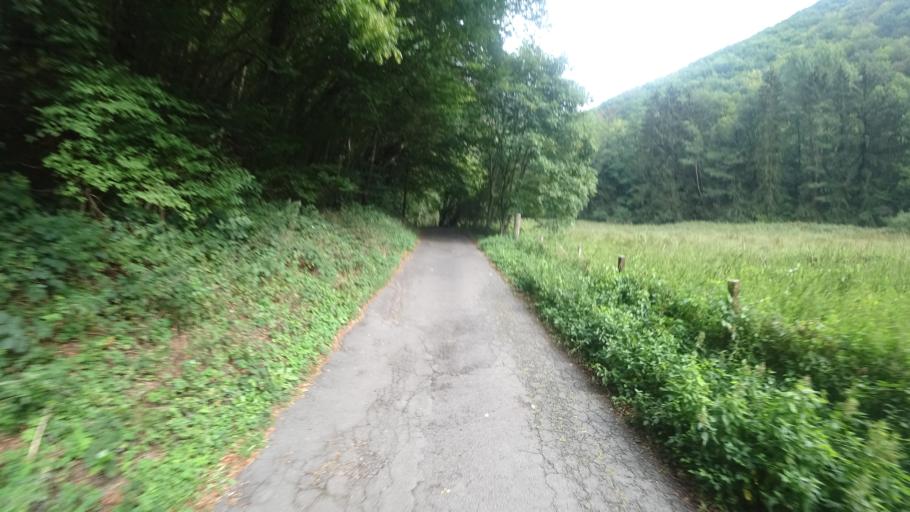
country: DE
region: Rheinland-Pfalz
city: Beulich
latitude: 50.2040
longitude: 7.4569
